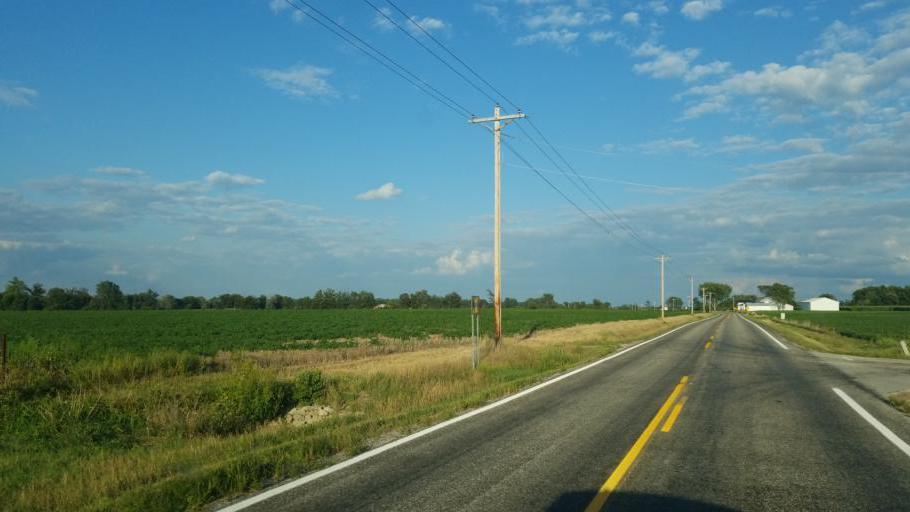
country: US
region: Ohio
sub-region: Huron County
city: Willard
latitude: 41.1067
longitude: -82.7690
